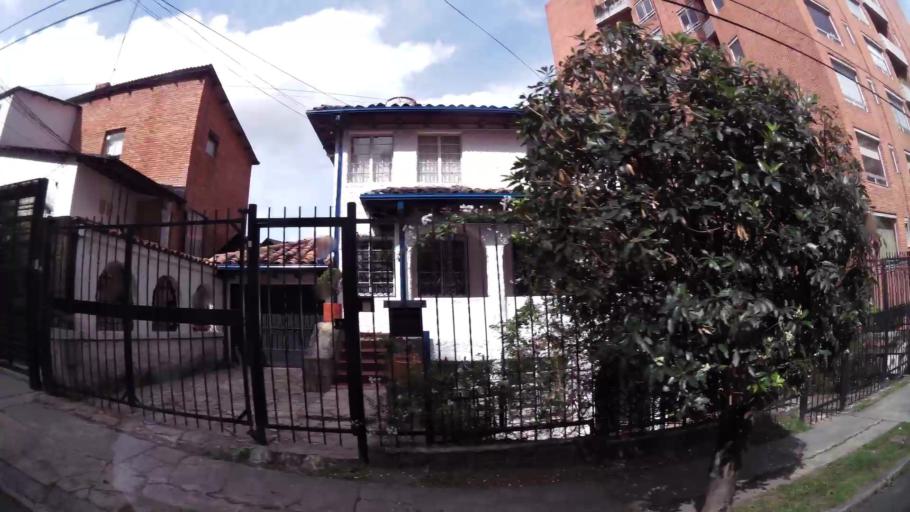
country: CO
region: Bogota D.C.
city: Barrio San Luis
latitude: 4.6560
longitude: -74.0507
